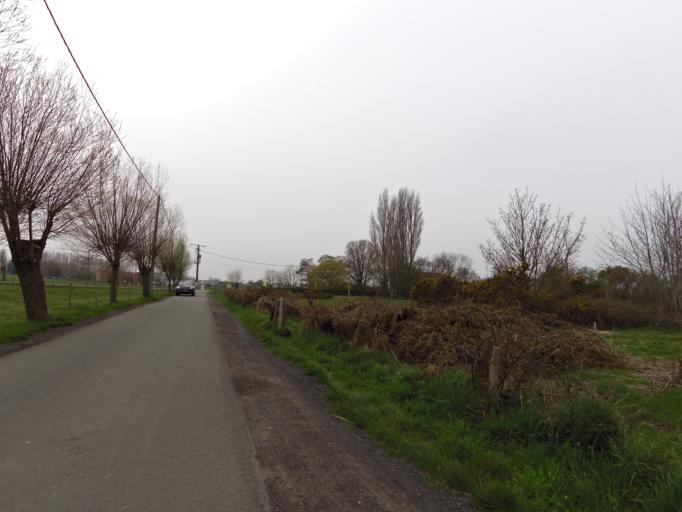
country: BE
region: Flanders
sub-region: Provincie West-Vlaanderen
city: Nieuwpoort
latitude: 51.1481
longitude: 2.7706
